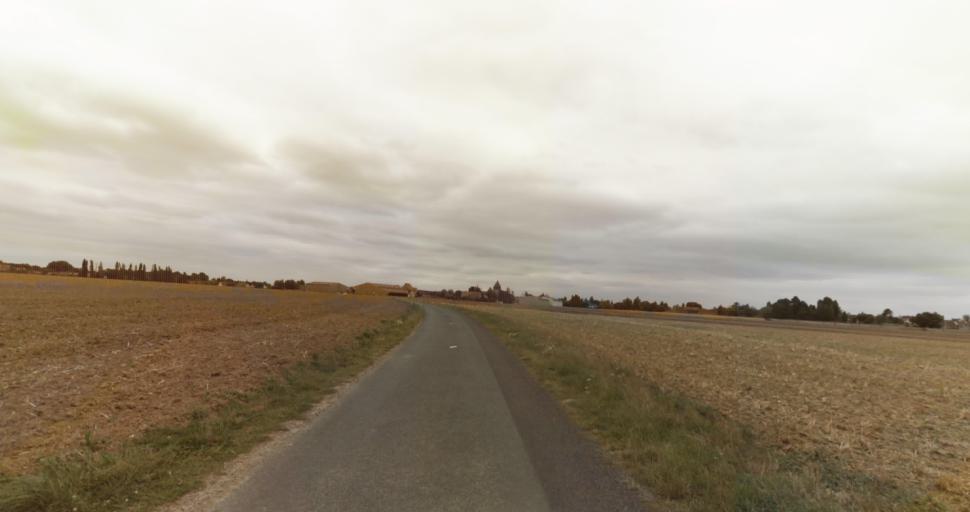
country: FR
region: Haute-Normandie
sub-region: Departement de l'Eure
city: Evreux
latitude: 48.9682
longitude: 1.2194
